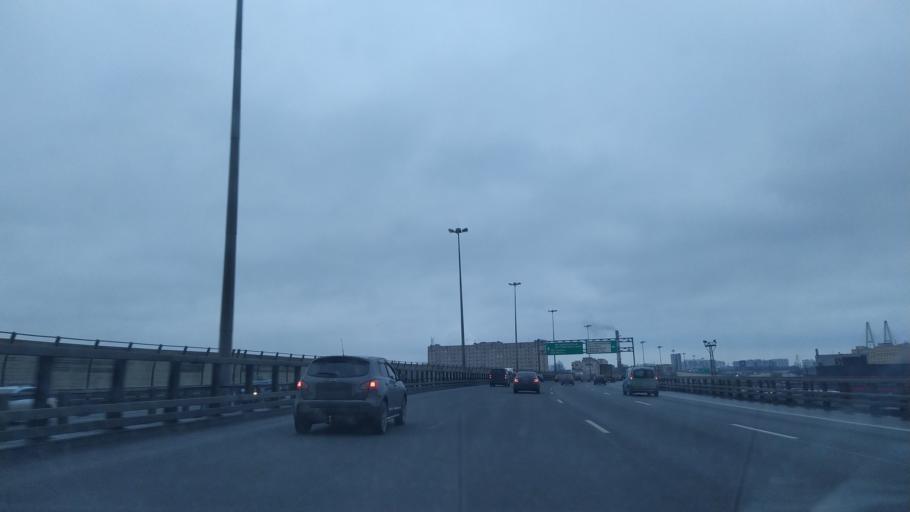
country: RU
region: St.-Petersburg
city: Obukhovo
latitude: 59.8473
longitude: 30.4611
